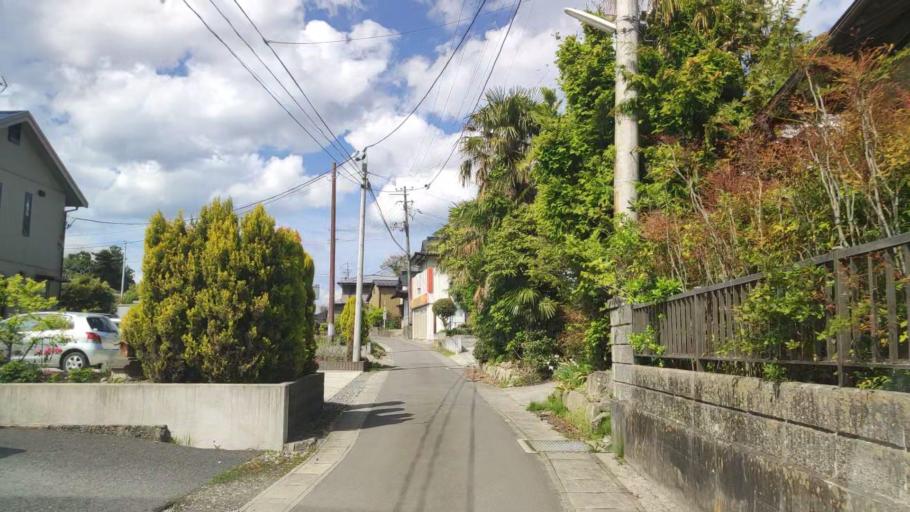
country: JP
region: Miyagi
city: Matsushima
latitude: 38.3370
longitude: 141.1436
